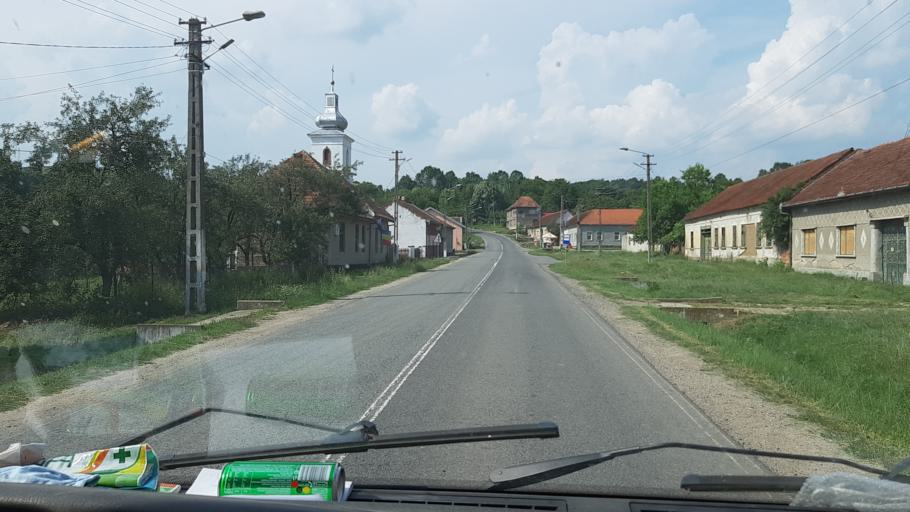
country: RO
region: Caras-Severin
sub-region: Comuna Farliug
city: Farliug
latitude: 45.5099
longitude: 21.8761
